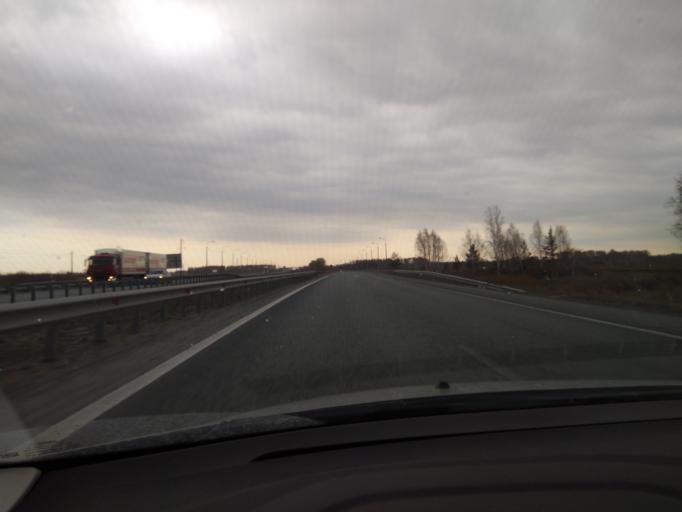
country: RU
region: Chelyabinsk
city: Kunashak
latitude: 55.7574
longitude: 61.2226
